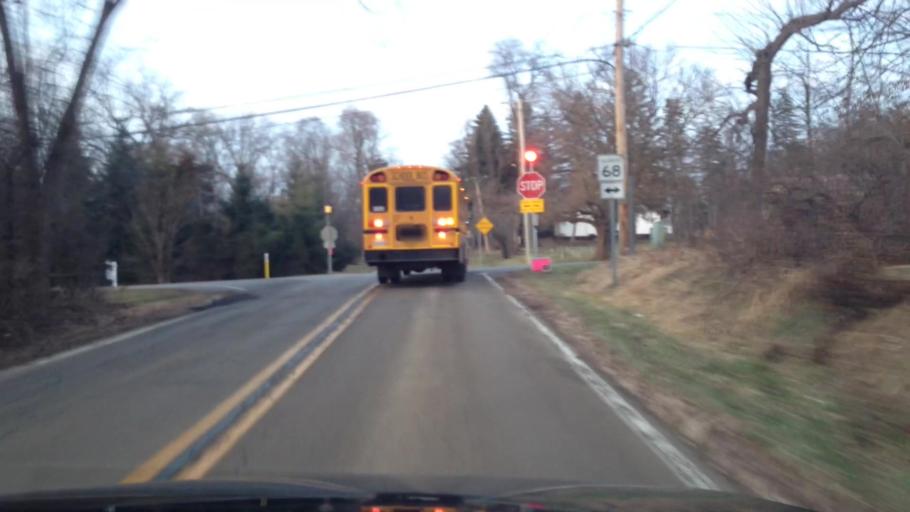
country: US
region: Illinois
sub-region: Cook County
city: Barrington Hills
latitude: 42.1101
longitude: -88.1947
